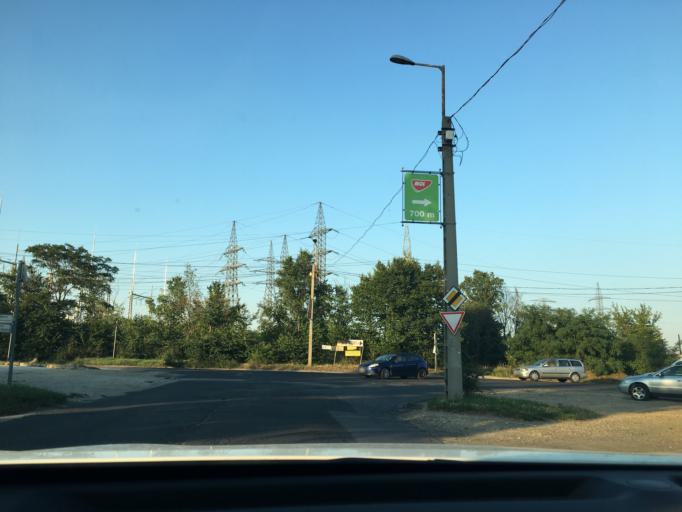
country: HU
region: Budapest
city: Budapest XVII. keruelet
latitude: 47.4986
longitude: 19.2380
